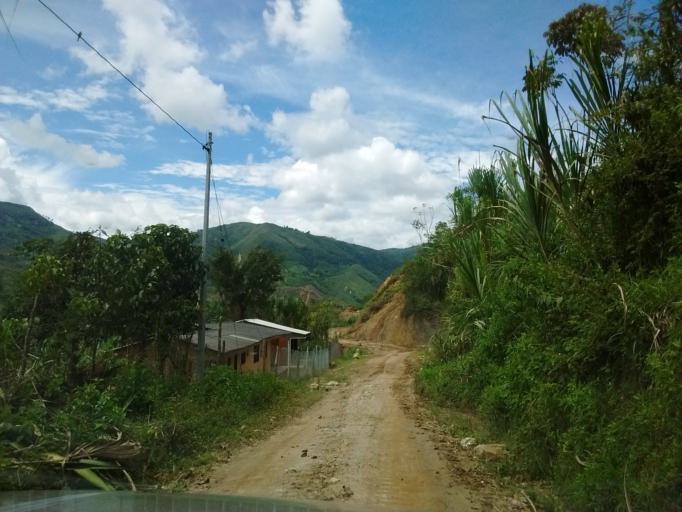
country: CO
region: Cauca
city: Morales
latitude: 2.6777
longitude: -76.7629
